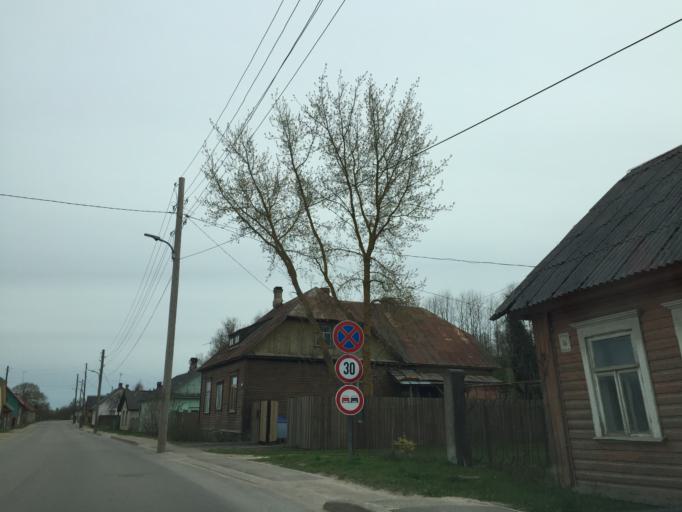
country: LV
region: Ludzas Rajons
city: Ludza
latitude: 56.5546
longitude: 27.7264
